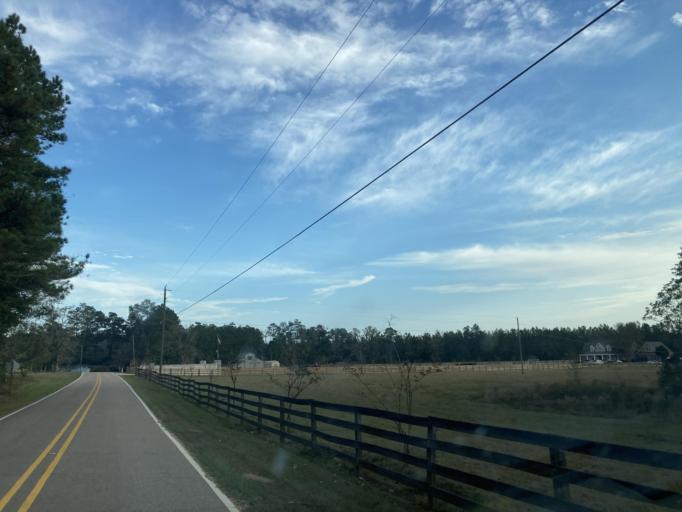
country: US
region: Mississippi
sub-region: Lamar County
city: Purvis
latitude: 31.1856
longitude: -89.3626
